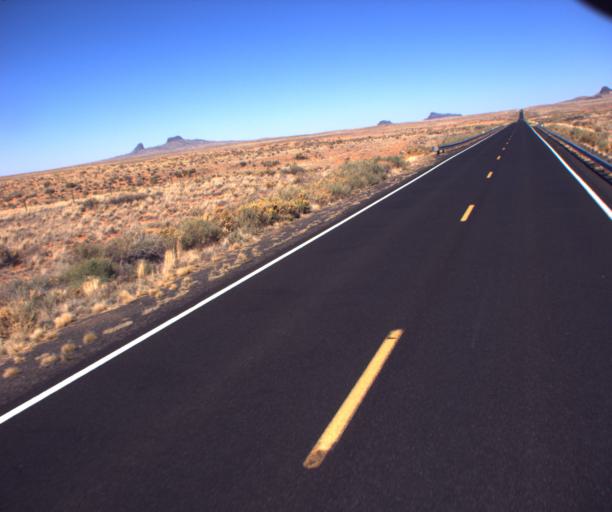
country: US
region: Arizona
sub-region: Navajo County
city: Dilkon
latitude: 35.3503
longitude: -110.4242
